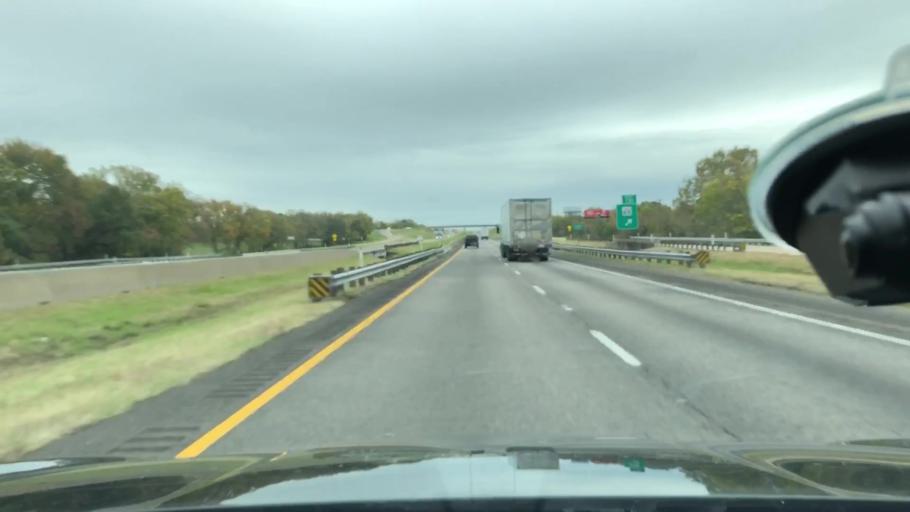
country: US
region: Texas
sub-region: Hopkins County
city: Sulphur Springs
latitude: 33.1467
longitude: -95.5023
